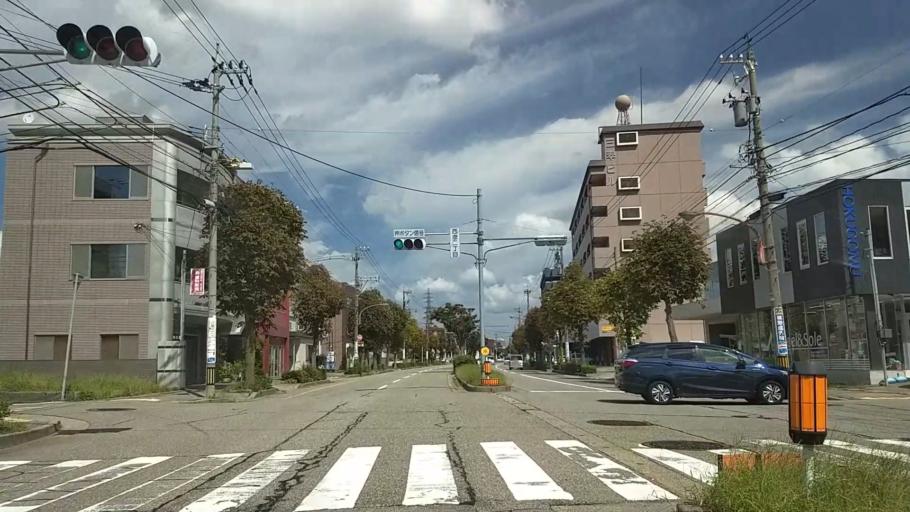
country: JP
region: Ishikawa
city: Kanazawa-shi
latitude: 36.5836
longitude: 136.6414
